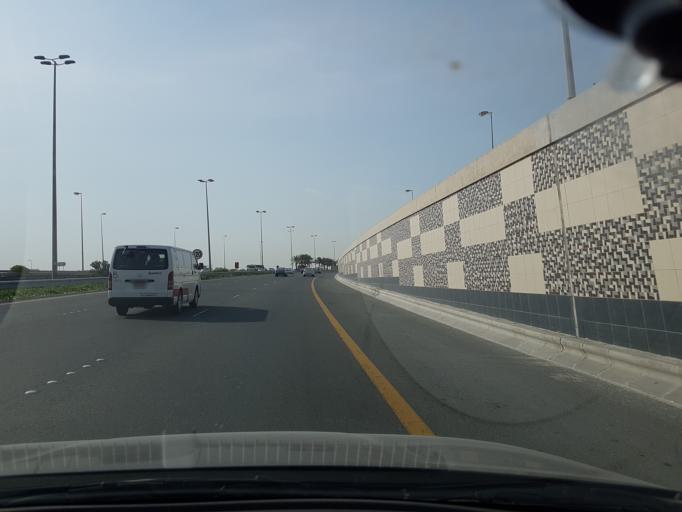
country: BH
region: Central Governorate
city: Madinat Hamad
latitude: 26.1188
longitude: 50.5092
